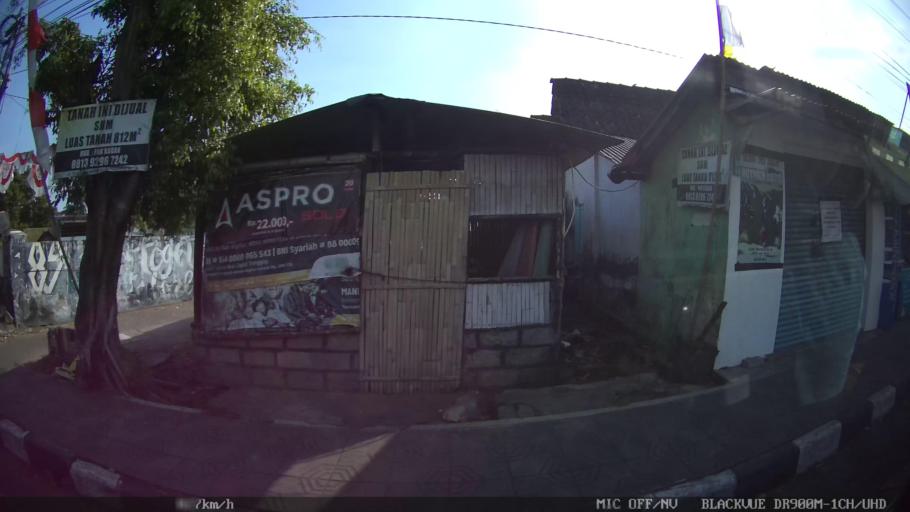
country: ID
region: Daerah Istimewa Yogyakarta
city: Yogyakarta
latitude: -7.8187
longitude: 110.3875
